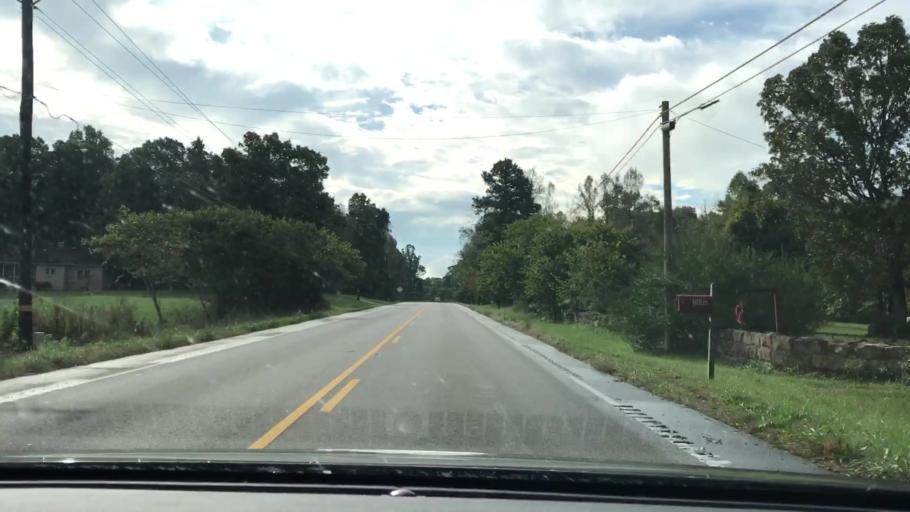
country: US
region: Tennessee
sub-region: Fentress County
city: Jamestown
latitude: 36.3784
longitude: -84.8753
